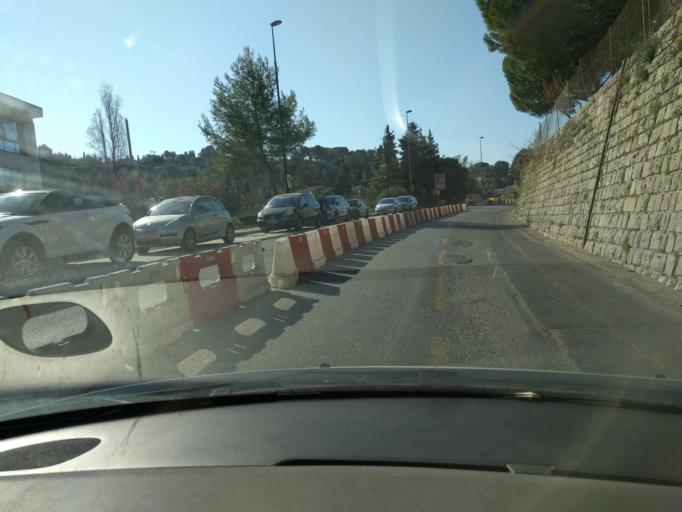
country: FR
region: Provence-Alpes-Cote d'Azur
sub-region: Departement des Alpes-Maritimes
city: Mougins
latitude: 43.6041
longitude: 6.9872
